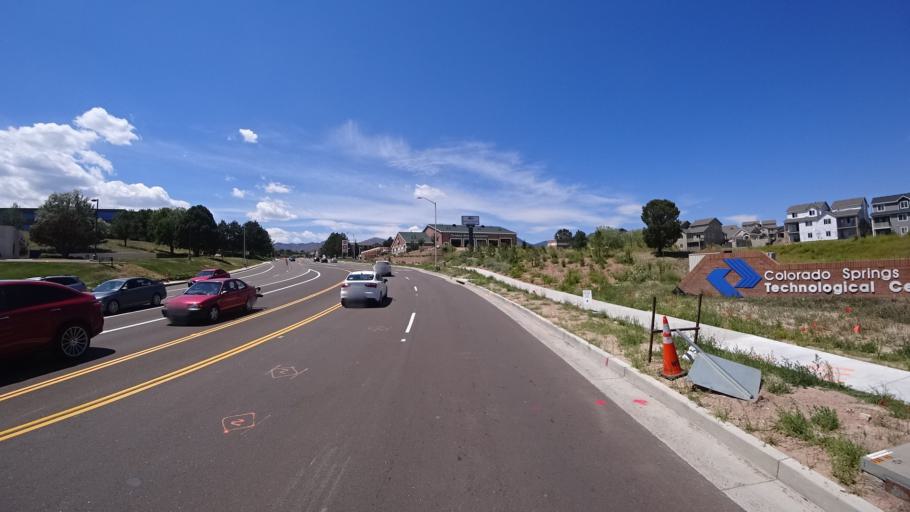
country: US
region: Colorado
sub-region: El Paso County
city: Colorado Springs
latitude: 38.9146
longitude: -104.8244
